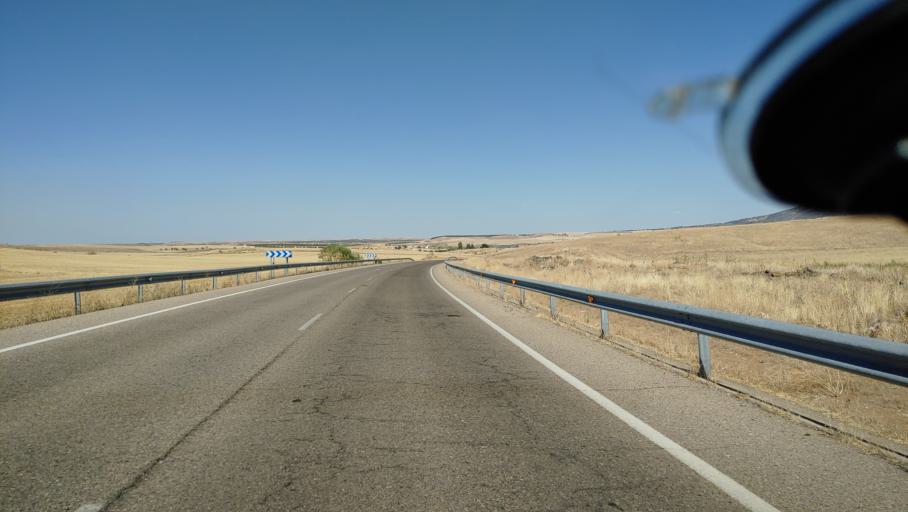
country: ES
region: Castille-La Mancha
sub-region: Province of Toledo
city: Pulgar
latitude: 39.7193
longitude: -4.1262
